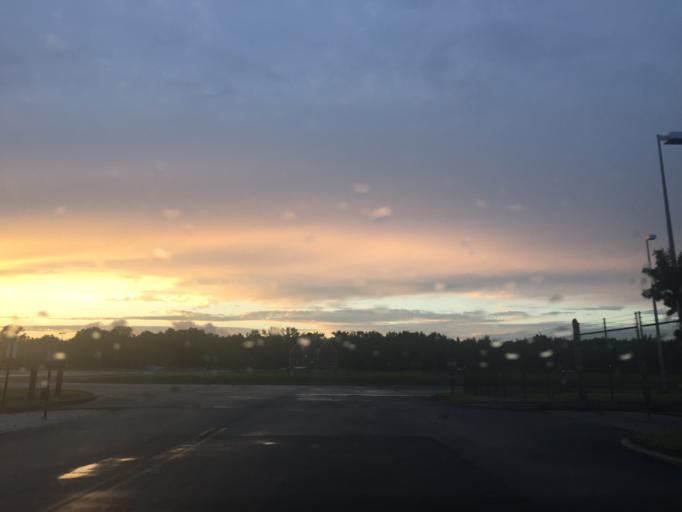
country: US
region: Maryland
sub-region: Baltimore County
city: Middle River
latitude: 39.3324
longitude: -76.4297
